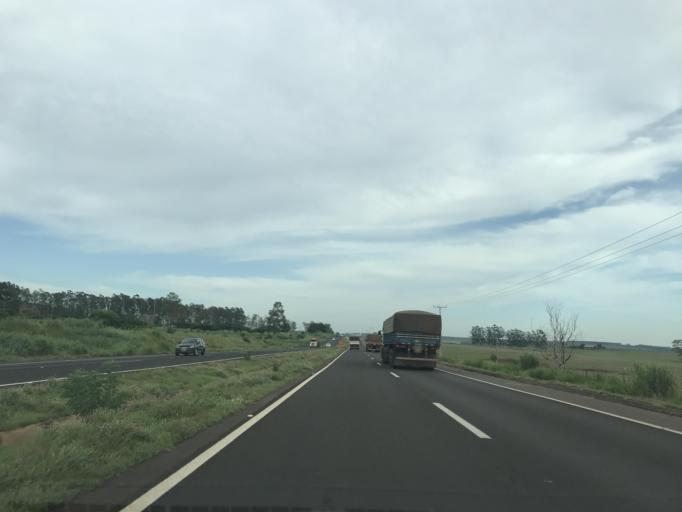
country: BR
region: Parana
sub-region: Alto Parana
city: Alto Parana
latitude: -23.1205
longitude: -52.3150
